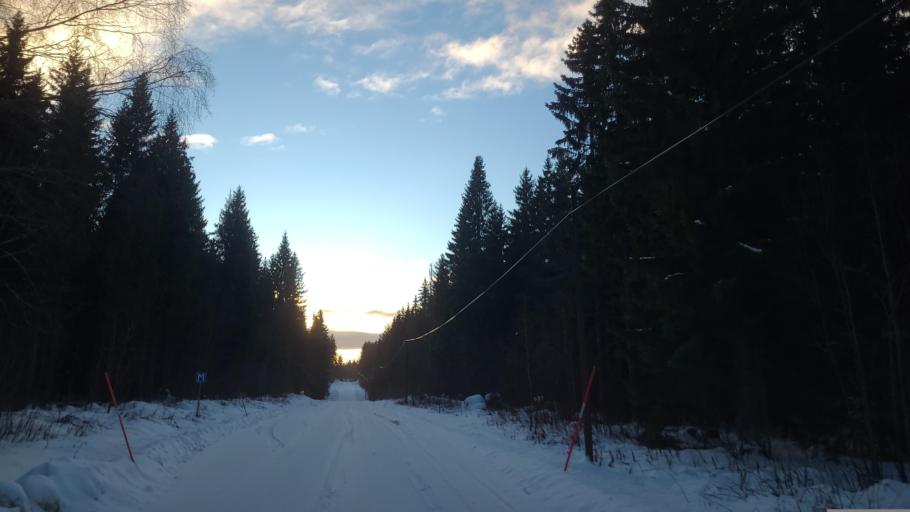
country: SE
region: Gaevleborg
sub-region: Bollnas Kommun
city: Kilafors
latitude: 61.3823
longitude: 16.6857
